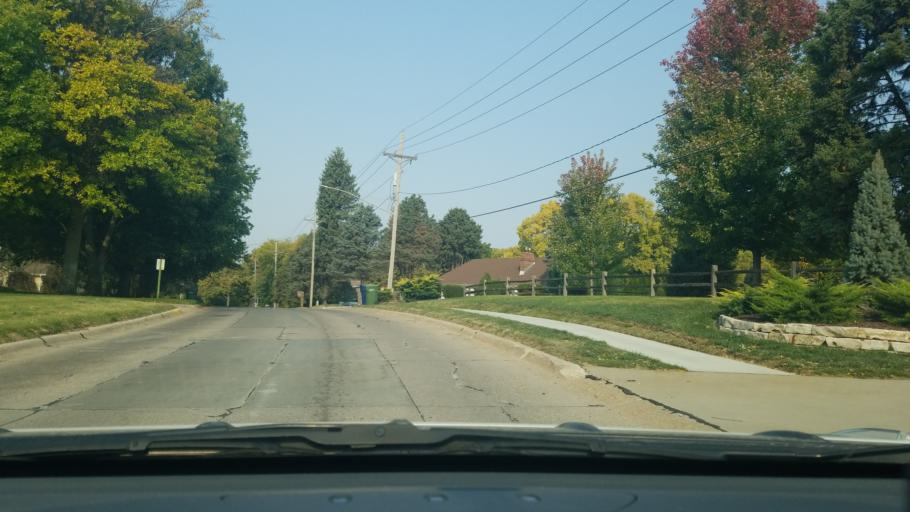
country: US
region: Nebraska
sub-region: Sarpy County
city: Bellevue
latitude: 41.1625
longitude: -95.9109
